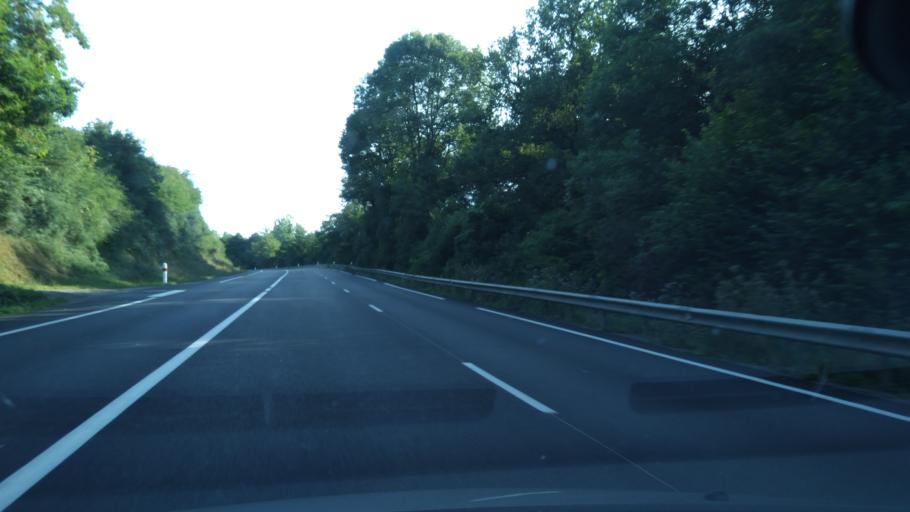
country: FR
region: Pays de la Loire
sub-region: Departement de la Mayenne
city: Entrammes
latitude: 47.9690
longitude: -0.7076
